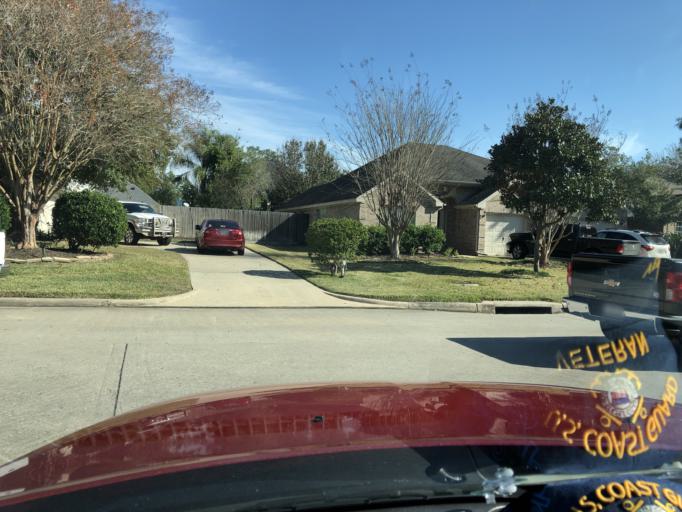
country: US
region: Texas
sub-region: Harris County
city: Tomball
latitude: 30.0213
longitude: -95.5562
